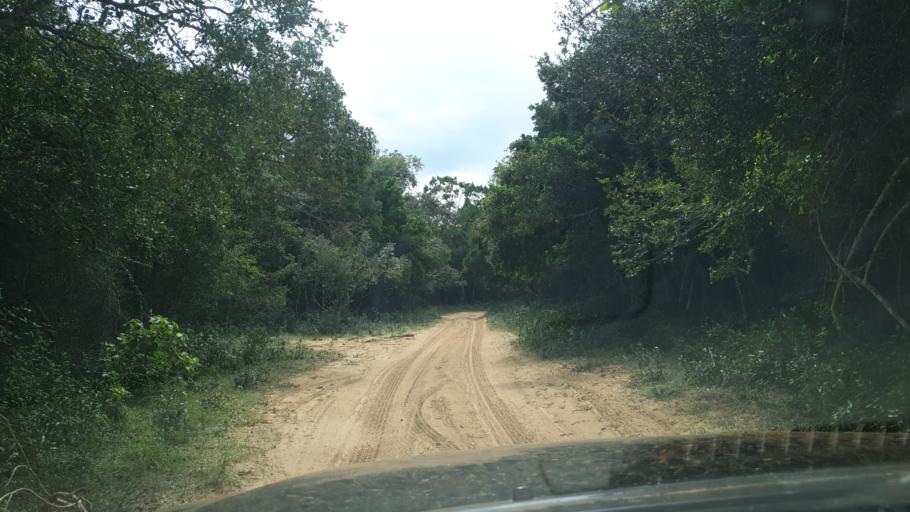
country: LK
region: North Western
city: Puttalam
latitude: 8.4171
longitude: 80.0006
